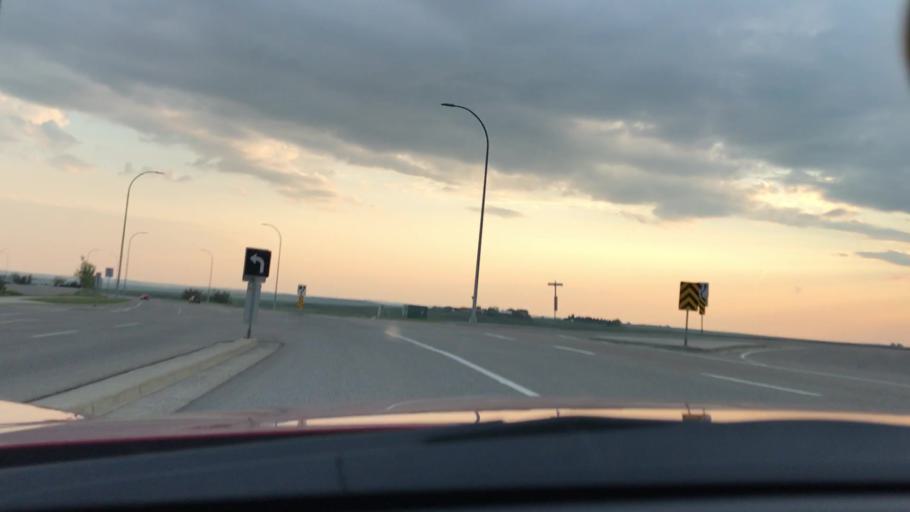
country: CA
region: Alberta
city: Airdrie
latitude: 51.2076
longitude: -113.9935
